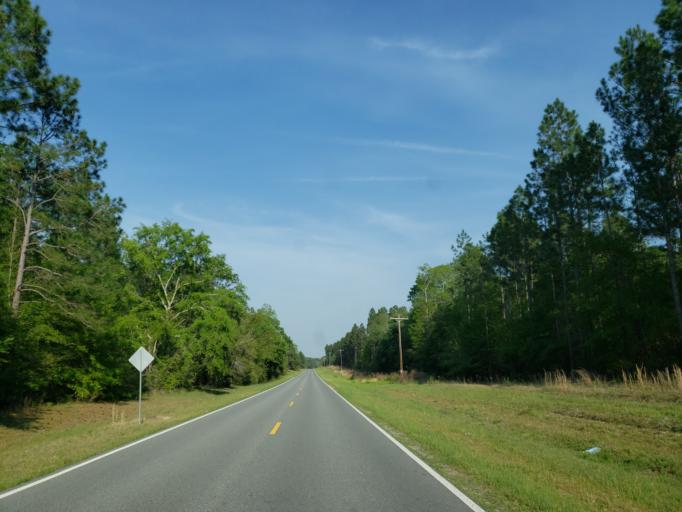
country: US
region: Georgia
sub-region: Tift County
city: Tifton
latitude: 31.5734
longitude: -83.5115
